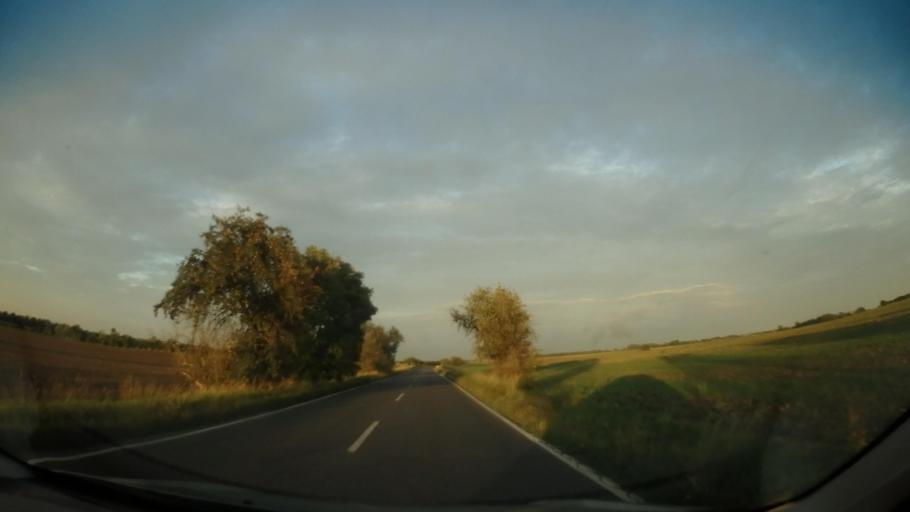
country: CZ
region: Central Bohemia
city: Milovice
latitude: 50.2247
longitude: 14.8996
